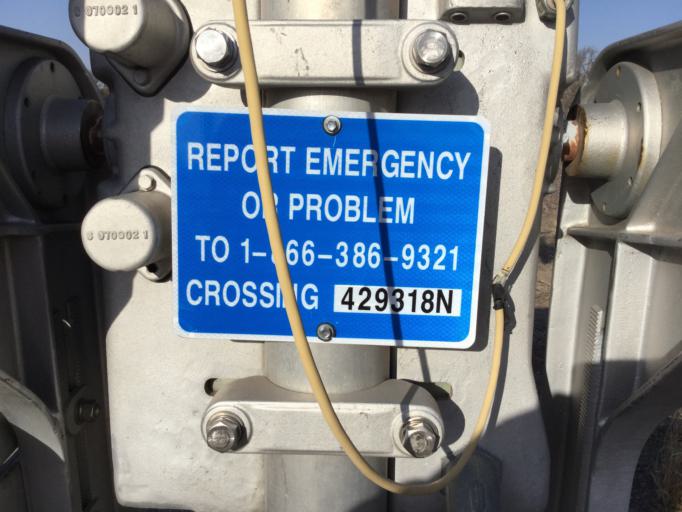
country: US
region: Kansas
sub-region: Rush County
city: La Crosse
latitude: 38.5307
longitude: -99.3037
